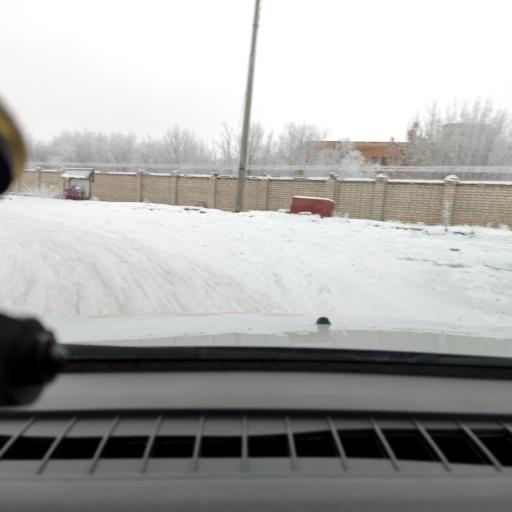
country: RU
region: Samara
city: Chapayevsk
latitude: 52.9963
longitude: 49.7864
